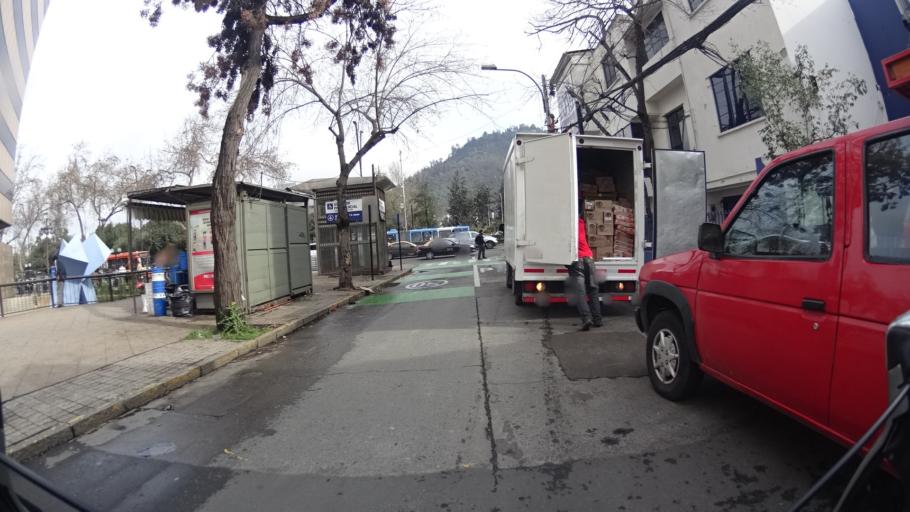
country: CL
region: Santiago Metropolitan
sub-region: Provincia de Santiago
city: Santiago
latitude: -33.4335
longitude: -70.6256
